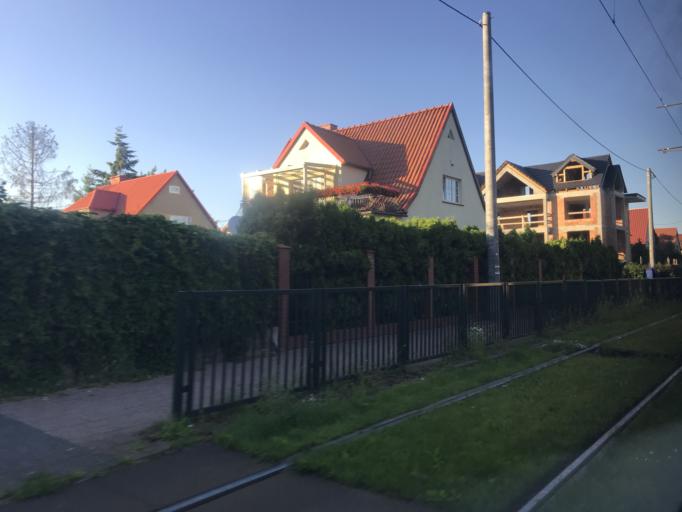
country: PL
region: Pomeranian Voivodeship
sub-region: Sopot
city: Sopot
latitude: 54.4214
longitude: 18.5872
